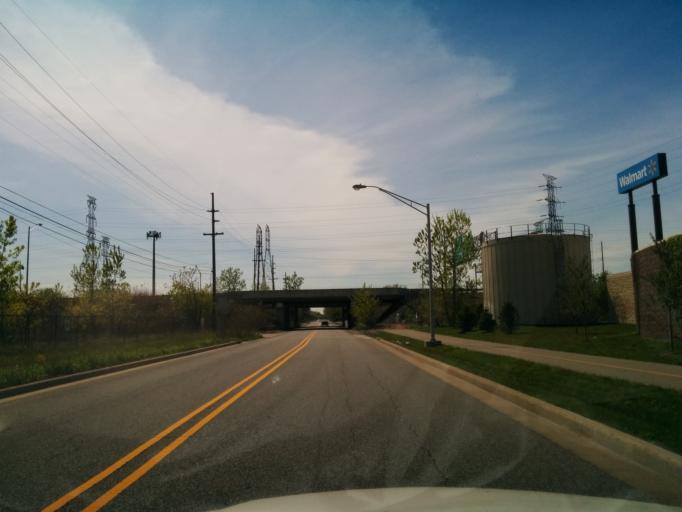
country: US
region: Indiana
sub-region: Lake County
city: Whiting
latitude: 41.6918
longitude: -87.5206
